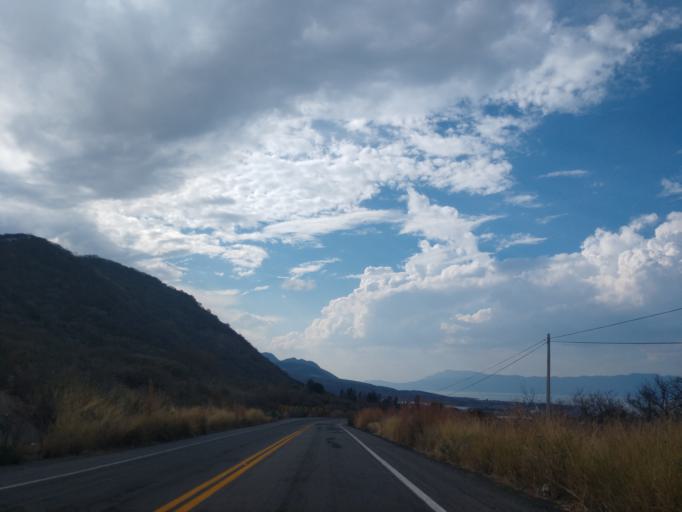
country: MX
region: Jalisco
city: Tizapan el Alto
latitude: 20.1293
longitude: -103.1645
